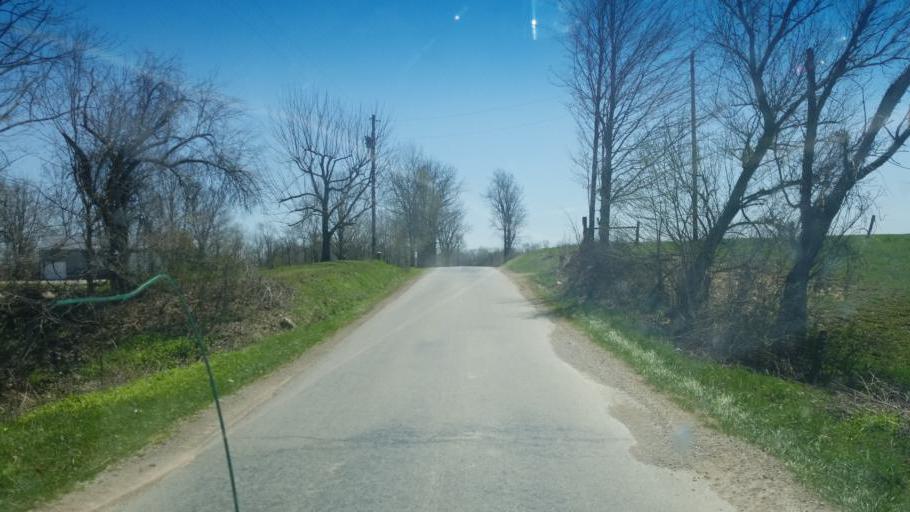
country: US
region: Ohio
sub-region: Huron County
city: Greenwich
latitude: 41.0615
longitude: -82.5121
